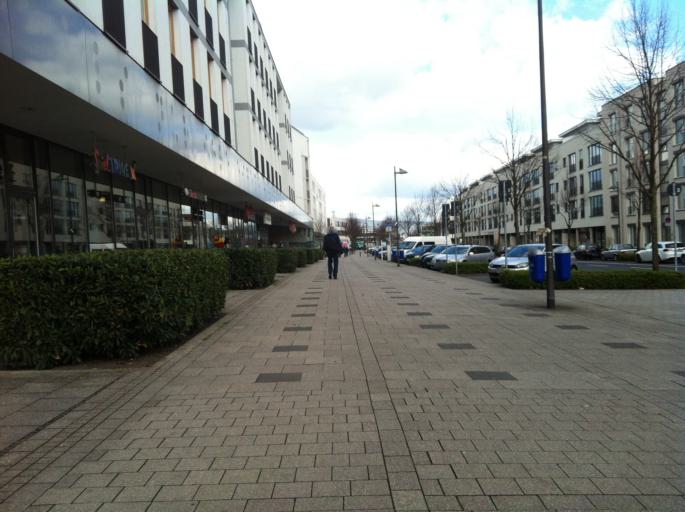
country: DE
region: Hesse
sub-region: Regierungsbezirk Darmstadt
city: Bad Homburg vor der Hoehe
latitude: 50.1773
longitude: 8.6296
